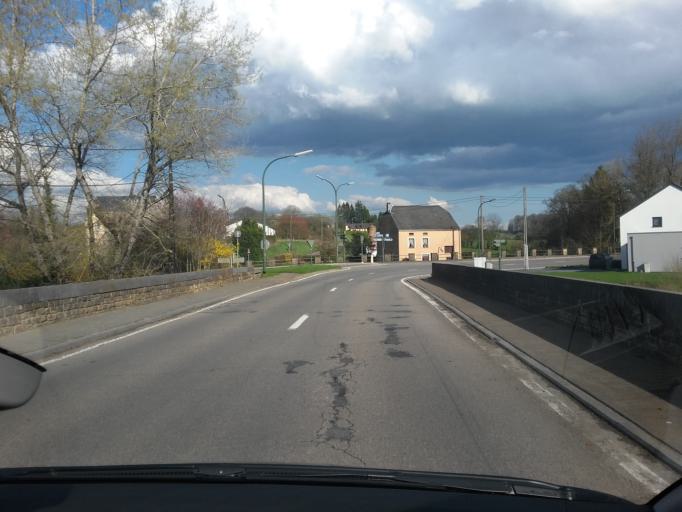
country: BE
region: Wallonia
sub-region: Province du Luxembourg
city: Florenville
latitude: 49.7102
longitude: 5.3263
